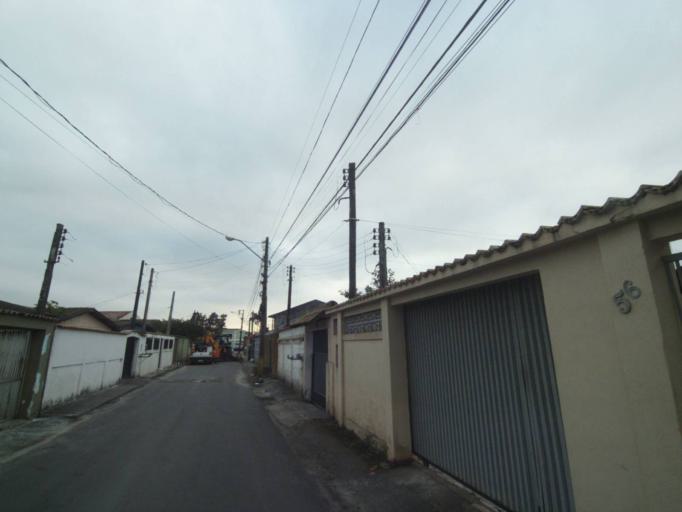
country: BR
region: Parana
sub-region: Paranagua
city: Paranagua
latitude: -25.5184
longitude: -48.5199
